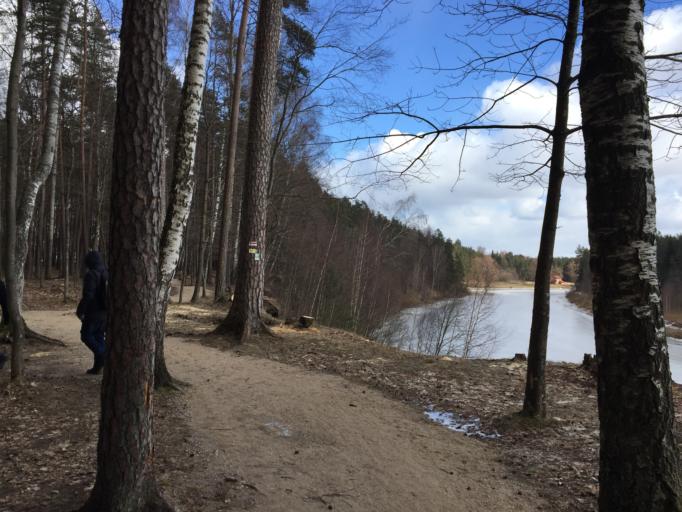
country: LV
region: Valmieras Rajons
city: Valmiera
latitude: 57.5408
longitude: 25.4441
